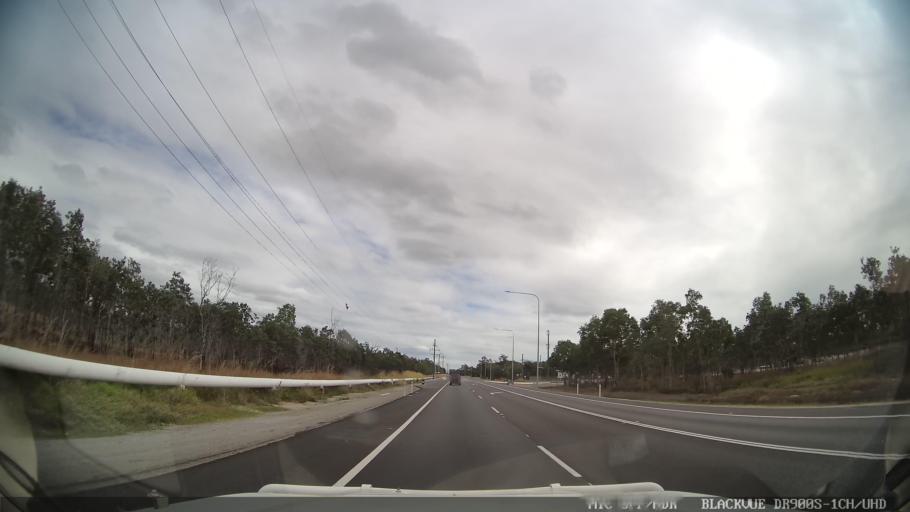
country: AU
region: Queensland
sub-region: Townsville
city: Bohle Plains
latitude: -19.1816
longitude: 146.5598
